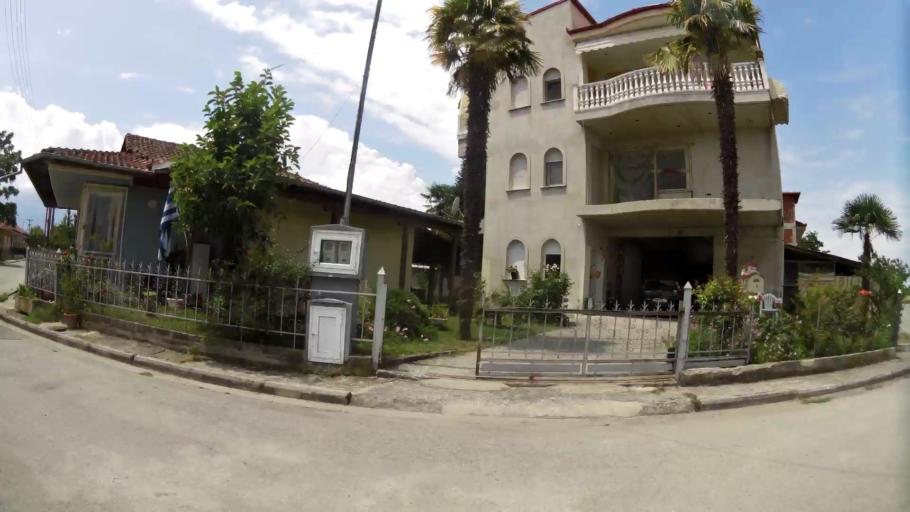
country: GR
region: Central Macedonia
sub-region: Nomos Pierias
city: Peristasi
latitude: 40.2637
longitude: 22.5365
